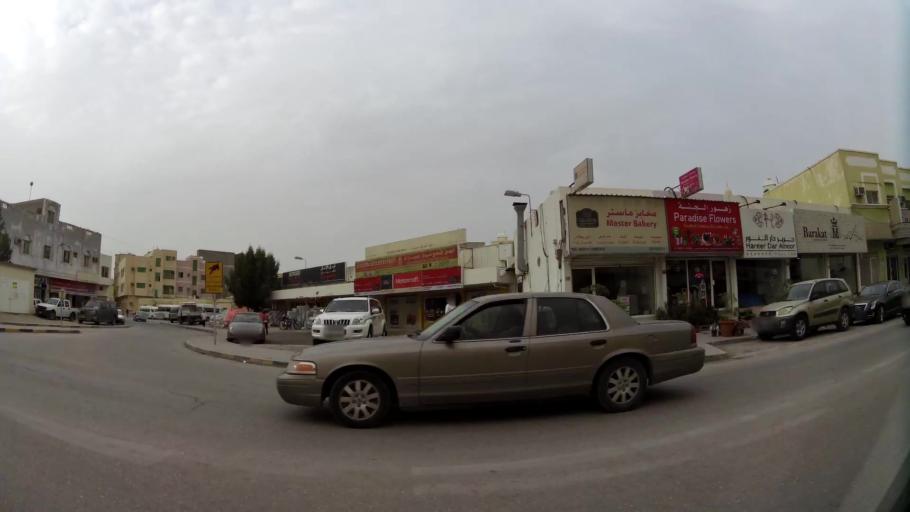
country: BH
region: Northern
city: Ar Rifa'
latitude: 26.1161
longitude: 50.5730
